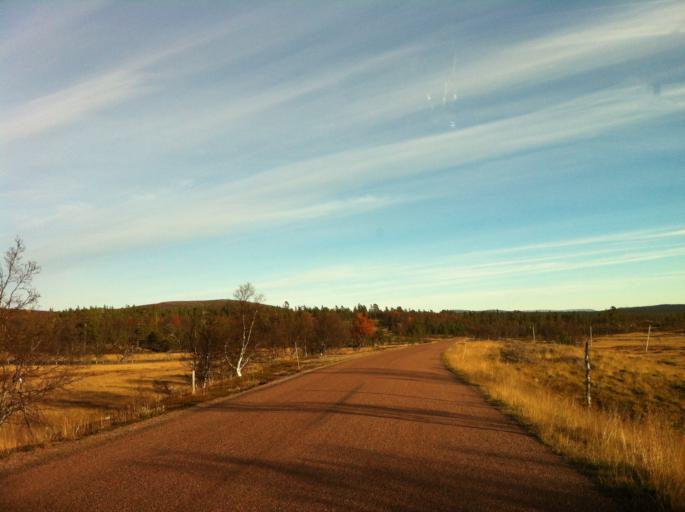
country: NO
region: Hedmark
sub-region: Engerdal
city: Engerdal
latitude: 62.0833
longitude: 12.1154
